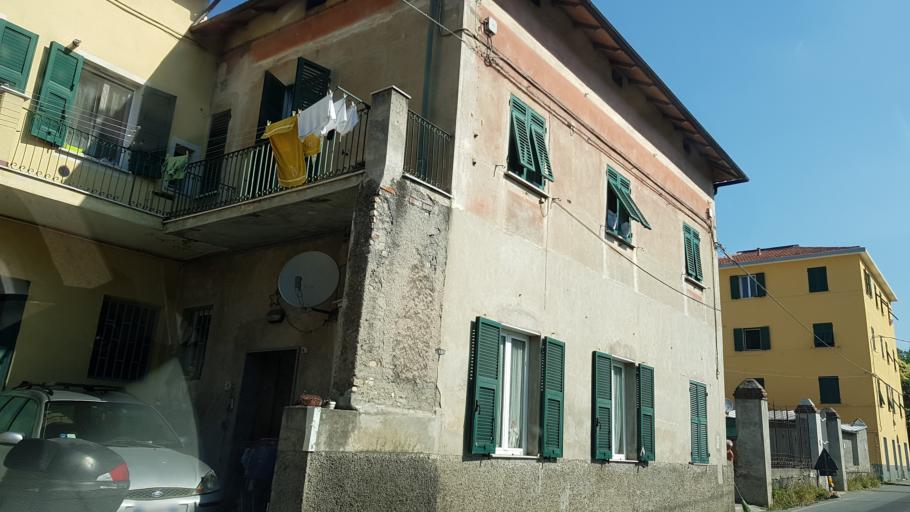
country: IT
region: Liguria
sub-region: Provincia di Genova
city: Manesseno
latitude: 44.4806
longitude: 8.9192
